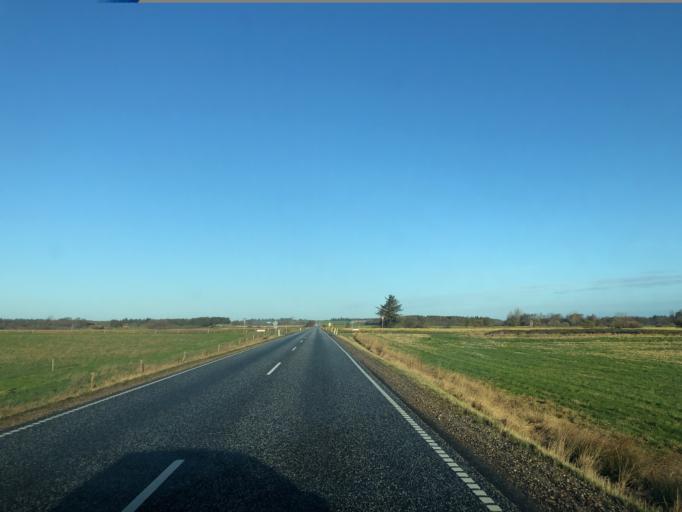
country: DK
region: Central Jutland
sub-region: Skive Kommune
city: Skive
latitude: 56.4841
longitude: 8.9575
